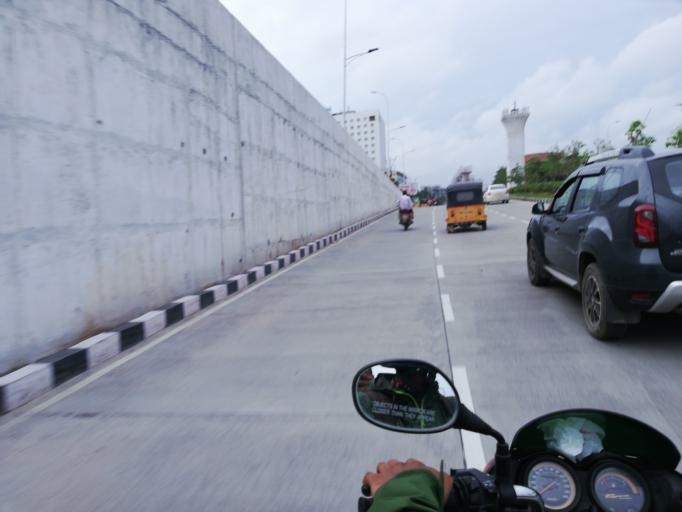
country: IN
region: Telangana
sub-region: Rangareddi
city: Kukatpalli
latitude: 17.4406
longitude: 78.3773
